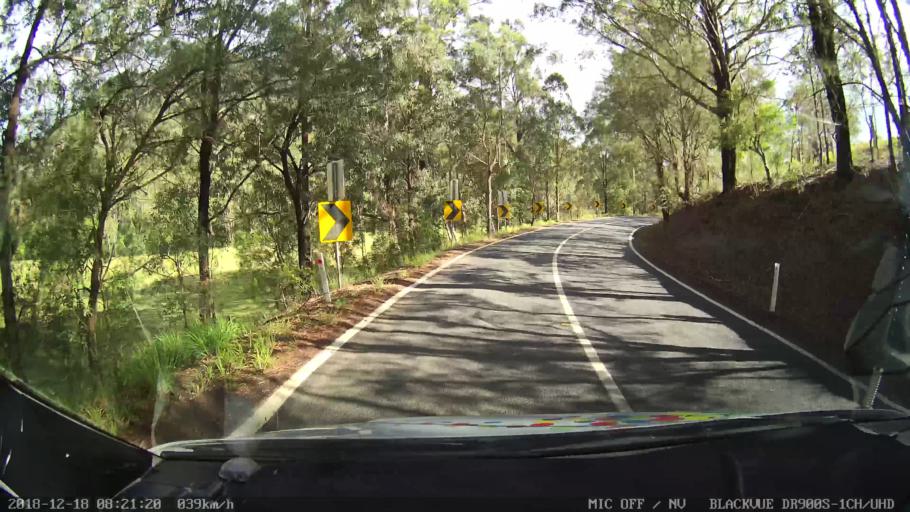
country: AU
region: New South Wales
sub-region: Kyogle
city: Kyogle
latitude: -28.3288
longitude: 152.7193
